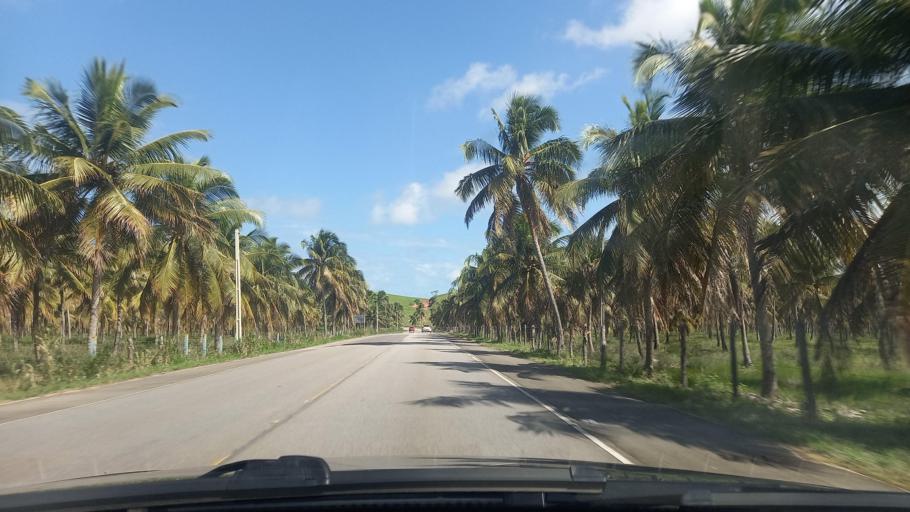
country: BR
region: Alagoas
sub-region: Marechal Deodoro
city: Marechal Deodoro
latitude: -9.8561
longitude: -35.9186
